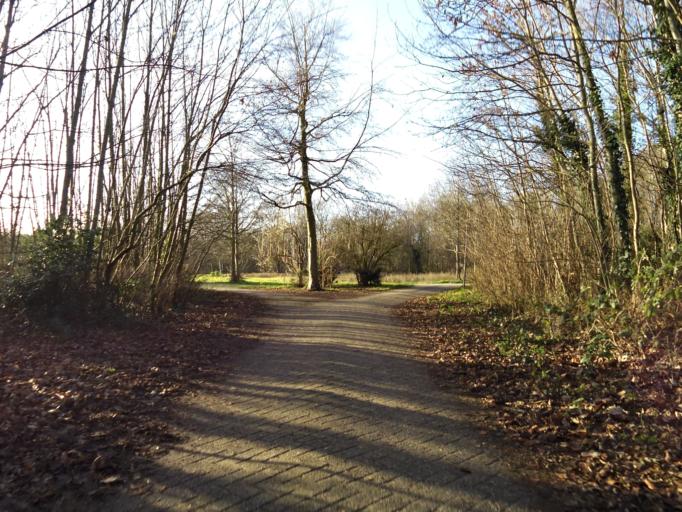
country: NL
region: South Holland
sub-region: Gemeente Noordwijkerhout
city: Noordwijkerhout
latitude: 52.2673
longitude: 4.4897
